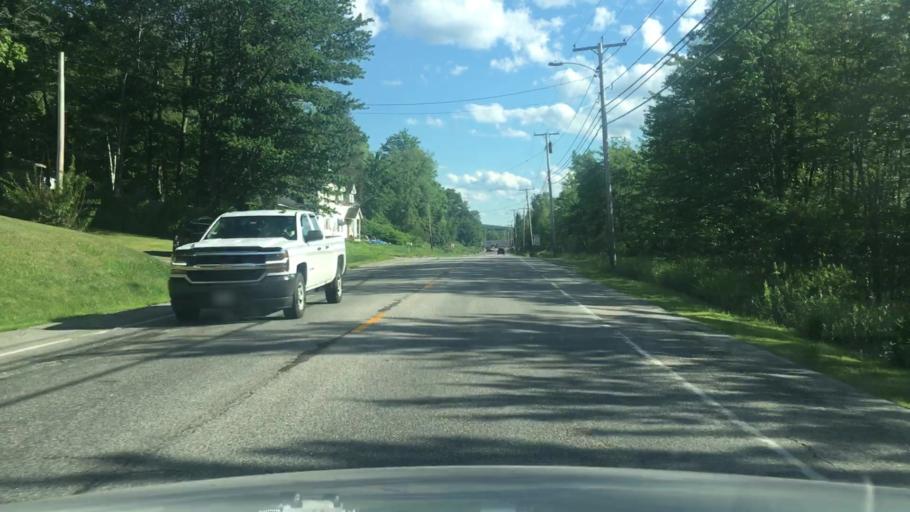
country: US
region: Maine
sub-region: Franklin County
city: Wilton
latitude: 44.5522
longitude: -70.2369
